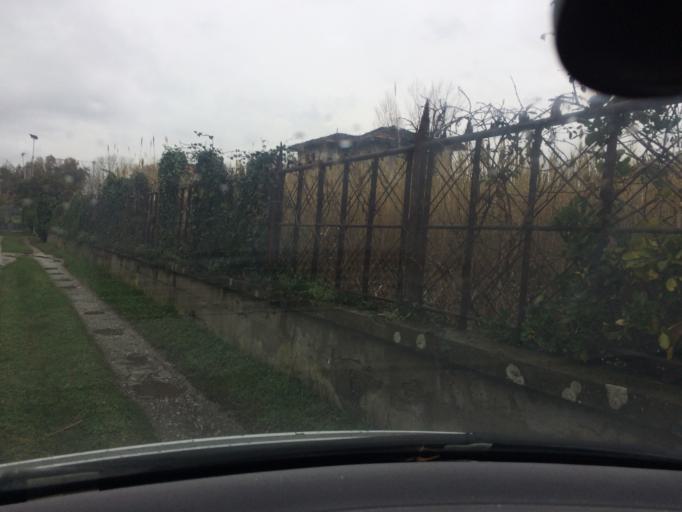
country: IT
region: Tuscany
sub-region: Provincia di Massa-Carrara
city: Massa
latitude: 44.0179
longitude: 10.0848
